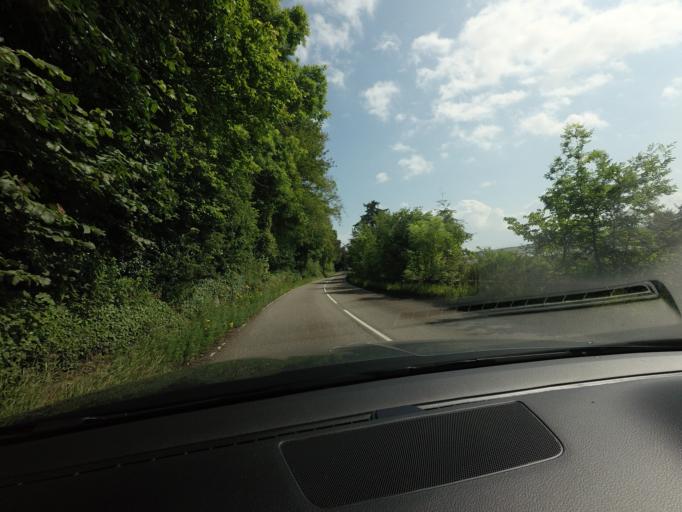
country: GB
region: Scotland
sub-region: Highland
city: Dingwall
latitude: 57.6151
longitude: -4.3979
